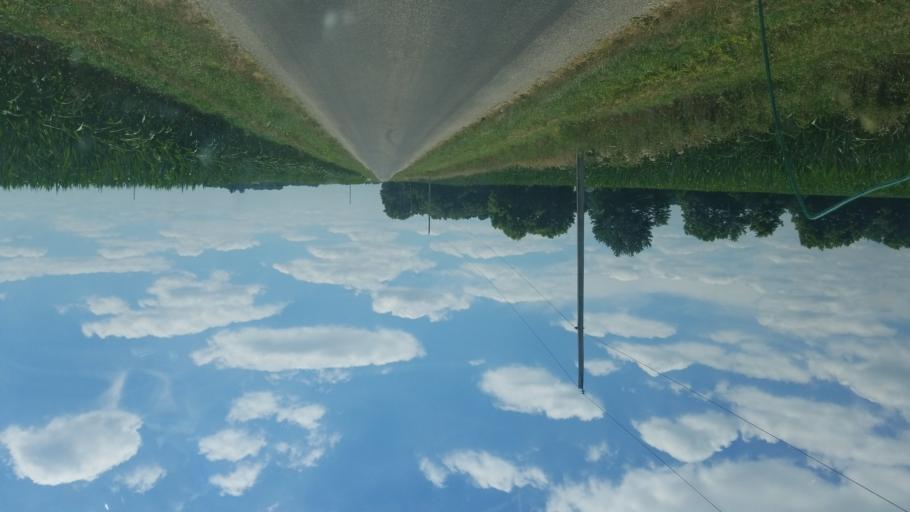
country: US
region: Ohio
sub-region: Defiance County
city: Hicksville
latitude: 41.3567
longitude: -84.6902
